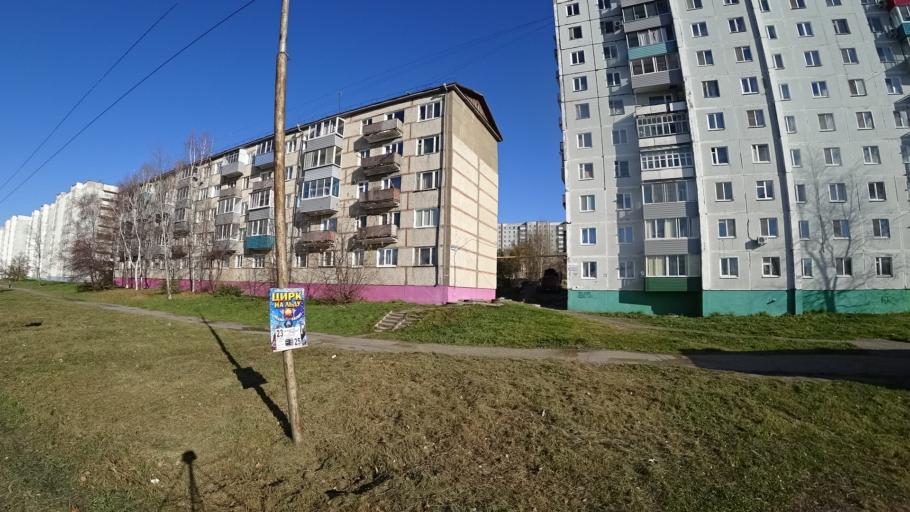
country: RU
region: Khabarovsk Krai
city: Amursk
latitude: 50.2458
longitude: 136.9161
